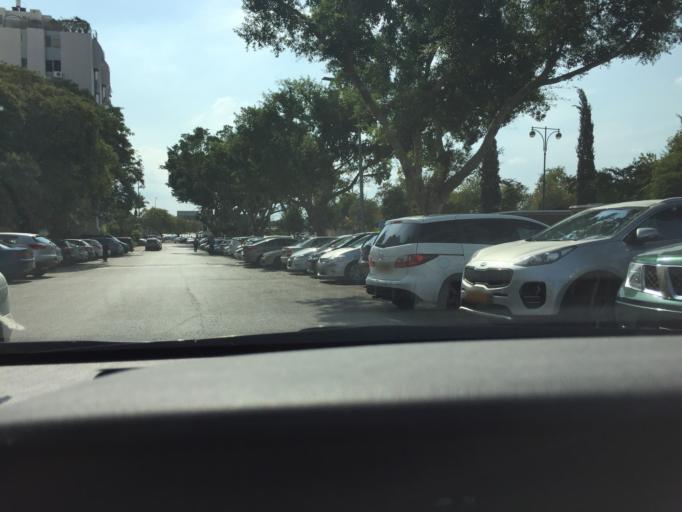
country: IL
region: Tel Aviv
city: Giv`at Shemu'el
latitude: 32.0676
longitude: 34.8455
